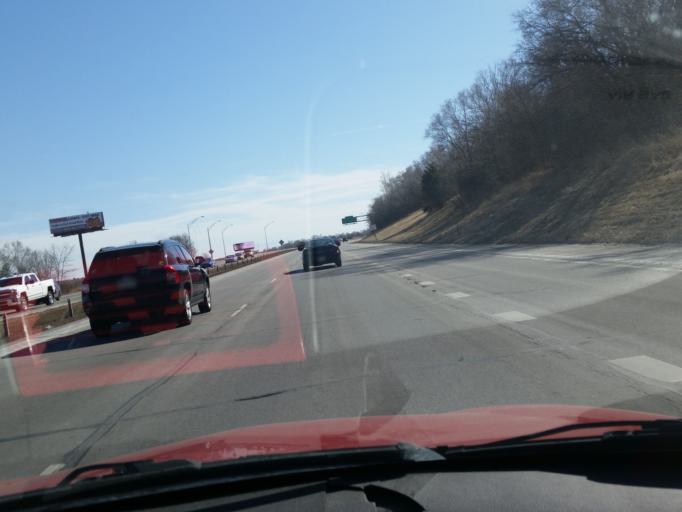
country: US
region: Nebraska
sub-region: Douglas County
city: Omaha
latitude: 41.1904
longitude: -95.9395
